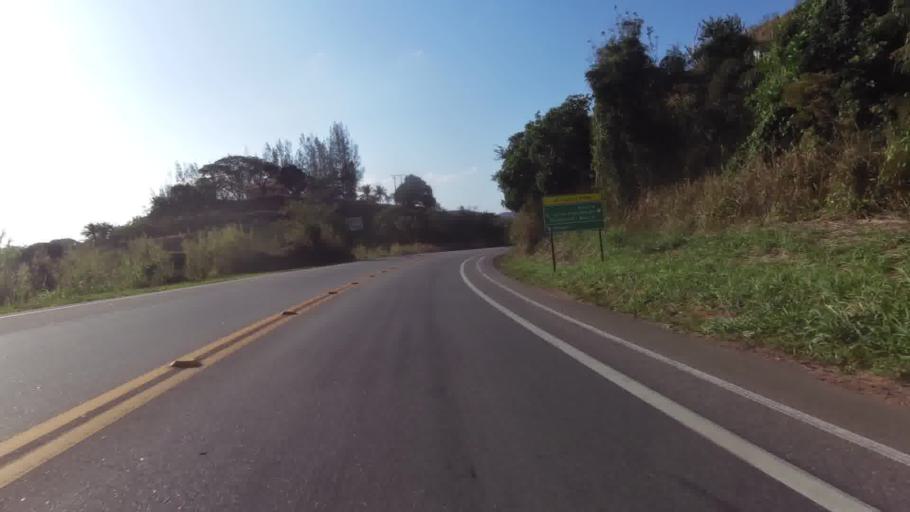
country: BR
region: Espirito Santo
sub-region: Mimoso Do Sul
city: Mimoso do Sul
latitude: -21.2019
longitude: -41.3009
